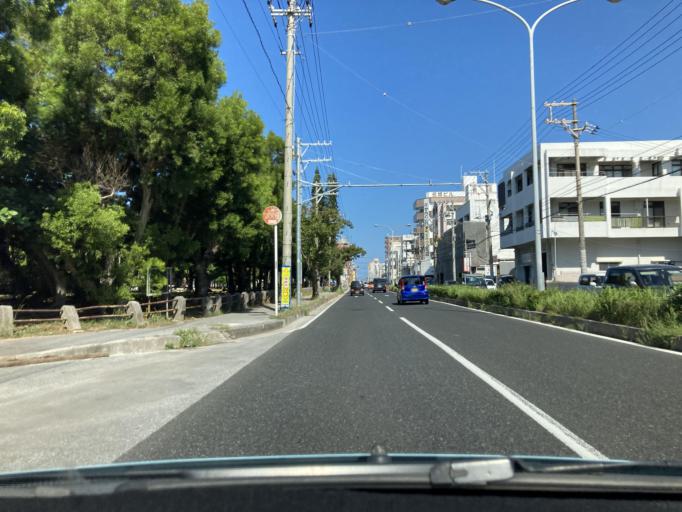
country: JP
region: Okinawa
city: Naha-shi
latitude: 26.2341
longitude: 127.6817
